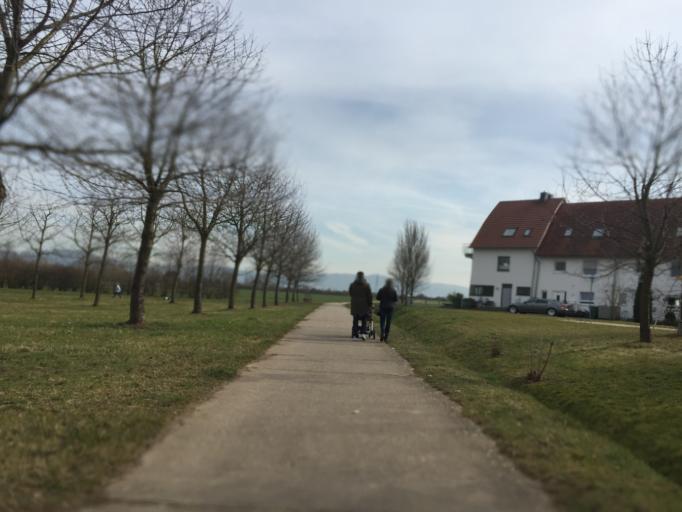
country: DE
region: Hesse
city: Viernheim
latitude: 49.5483
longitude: 8.6018
